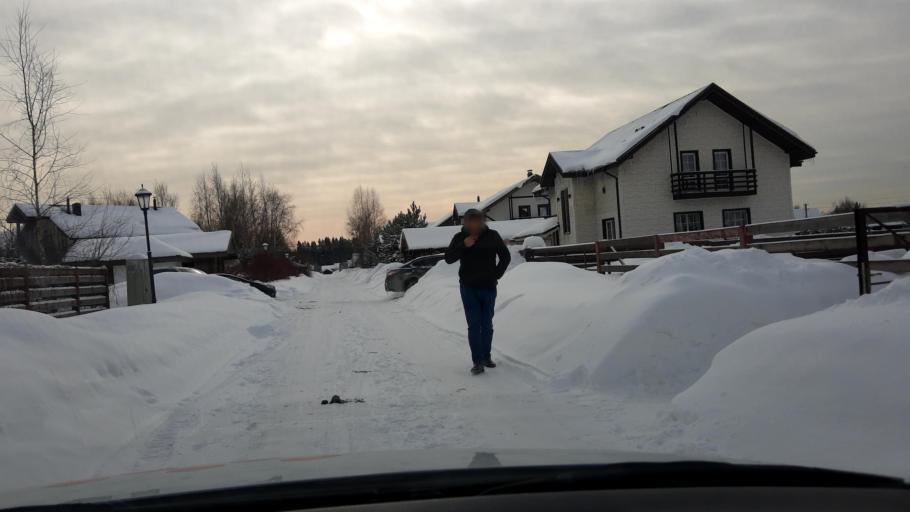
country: RU
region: Moskovskaya
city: Rumyantsevo
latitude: 55.9161
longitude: 36.5809
